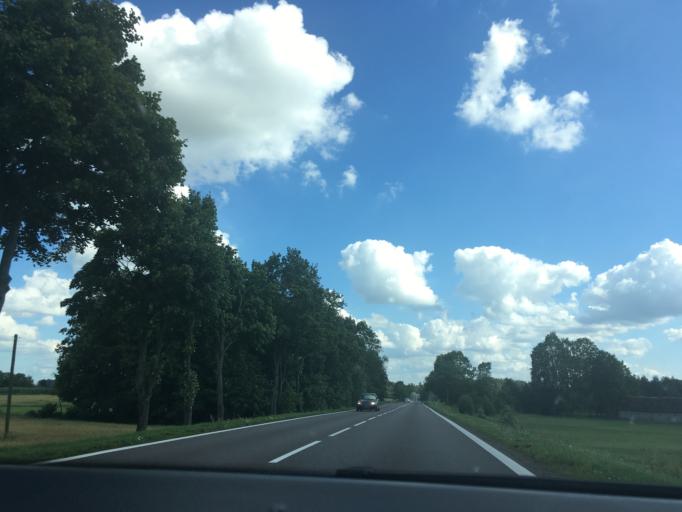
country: PL
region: Podlasie
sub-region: Powiat sokolski
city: Janow
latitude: 53.4203
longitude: 23.1116
